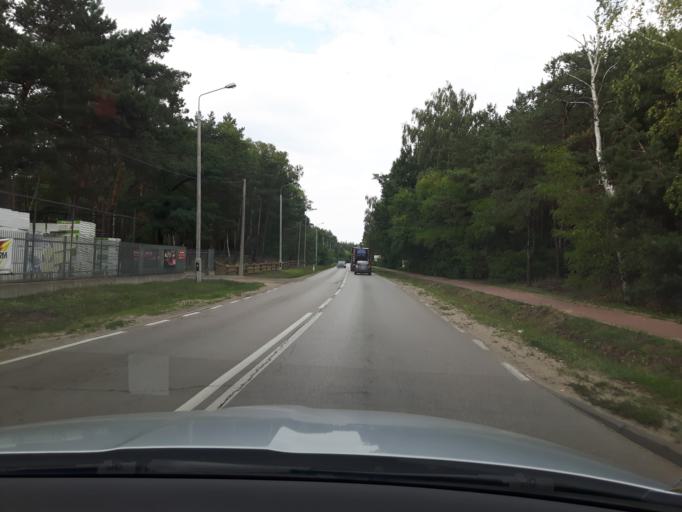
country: PL
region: Masovian Voivodeship
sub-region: Powiat legionowski
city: Stanislawow Pierwszy
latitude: 52.3795
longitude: 21.0292
